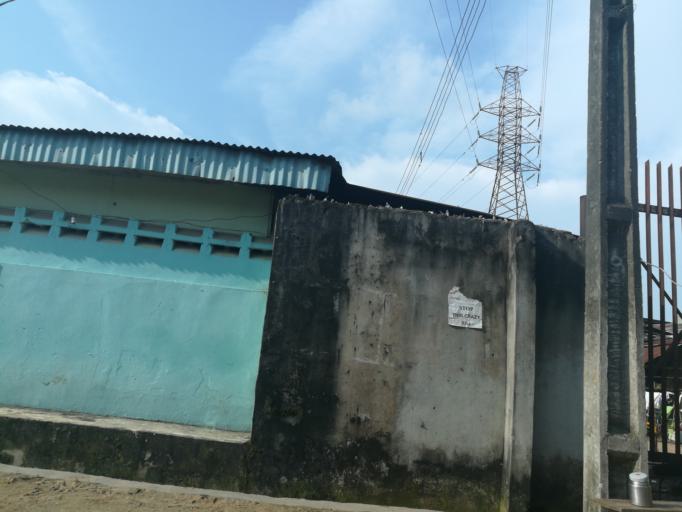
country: NG
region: Lagos
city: Ojota
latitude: 6.5924
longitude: 3.3997
